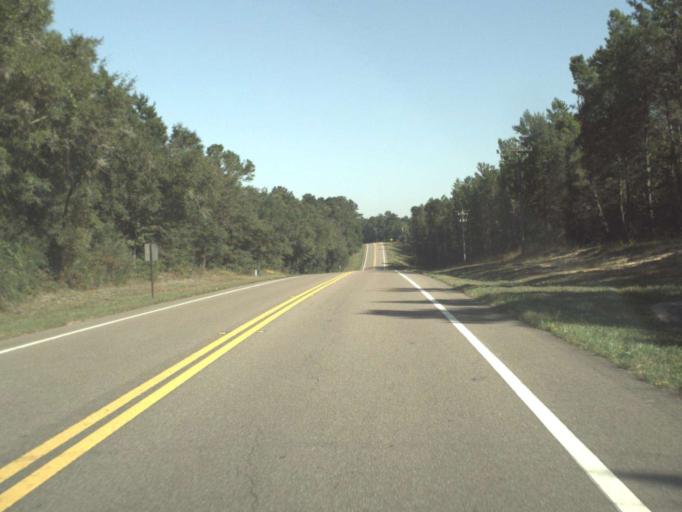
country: US
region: Florida
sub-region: Walton County
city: DeFuniak Springs
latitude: 30.5948
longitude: -85.9445
